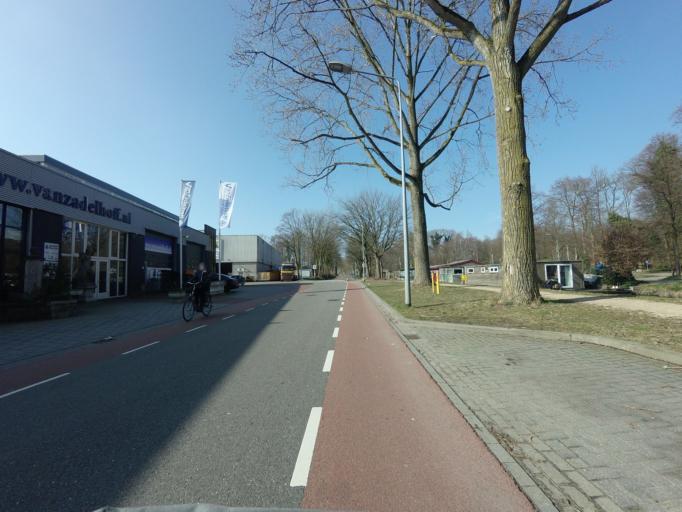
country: NL
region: North Holland
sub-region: Gemeente Wijdemeren
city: Nieuw-Loosdrecht
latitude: 52.2243
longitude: 5.1412
